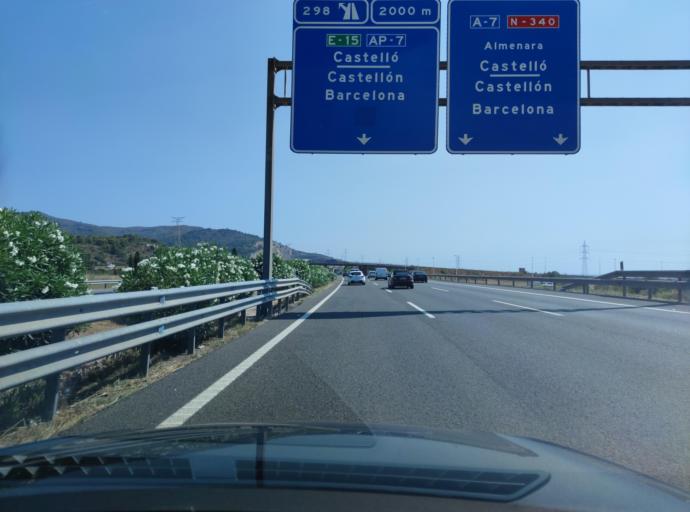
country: ES
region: Valencia
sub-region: Provincia de Valencia
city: Petres
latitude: 39.6893
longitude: -0.2873
